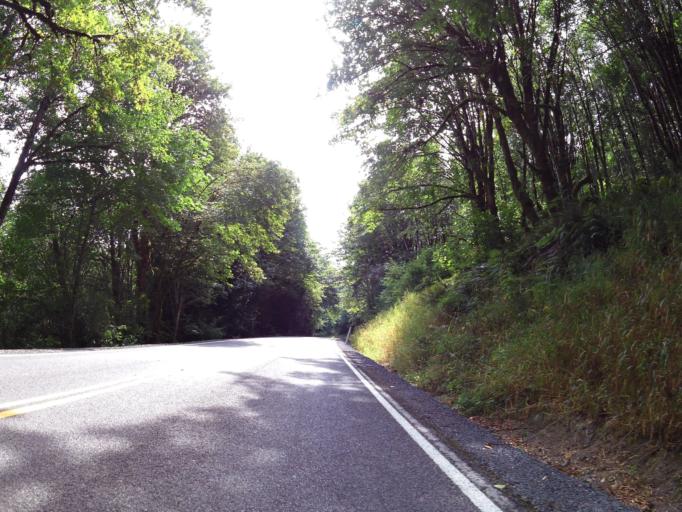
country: US
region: Washington
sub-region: Lewis County
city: Napavine
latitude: 46.5543
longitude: -122.9581
